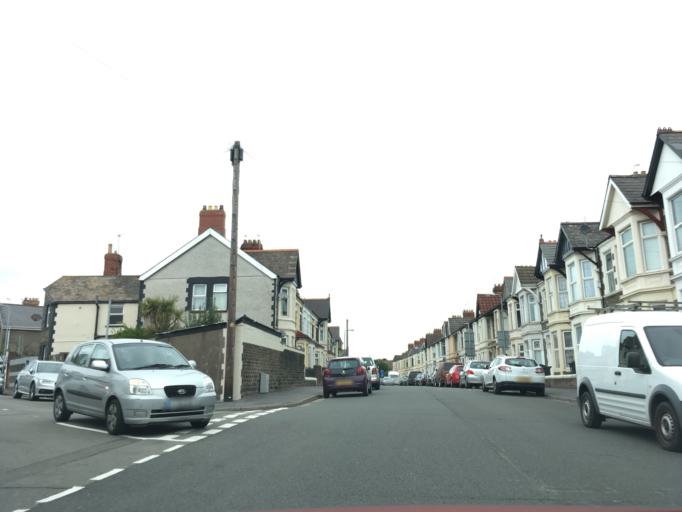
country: GB
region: Wales
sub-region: Cardiff
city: Cardiff
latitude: 51.4863
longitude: -3.1471
